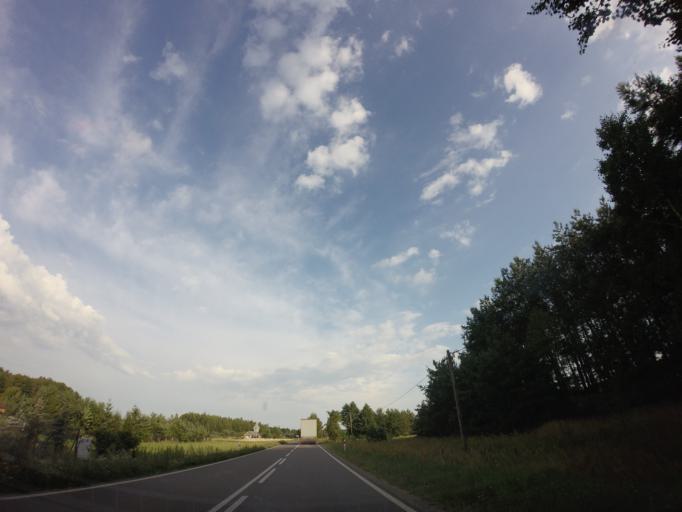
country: PL
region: Lublin Voivodeship
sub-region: Powiat lubartowski
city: Jeziorzany
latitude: 51.5764
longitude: 22.2863
